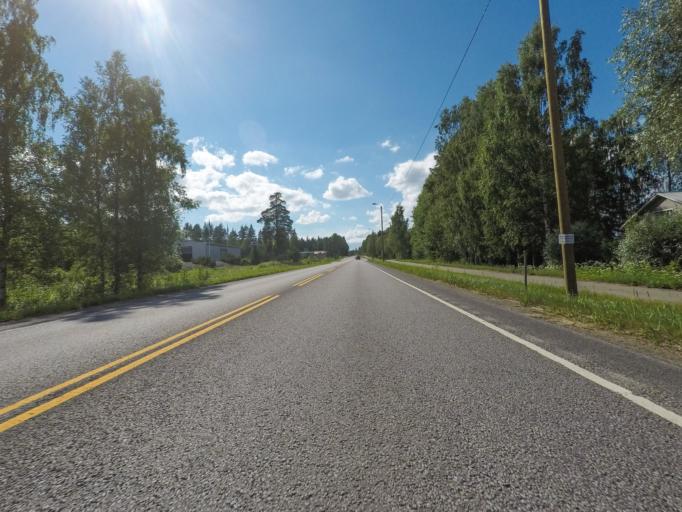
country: FI
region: Southern Savonia
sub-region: Savonlinna
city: Savonlinna
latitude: 61.8774
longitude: 28.9737
